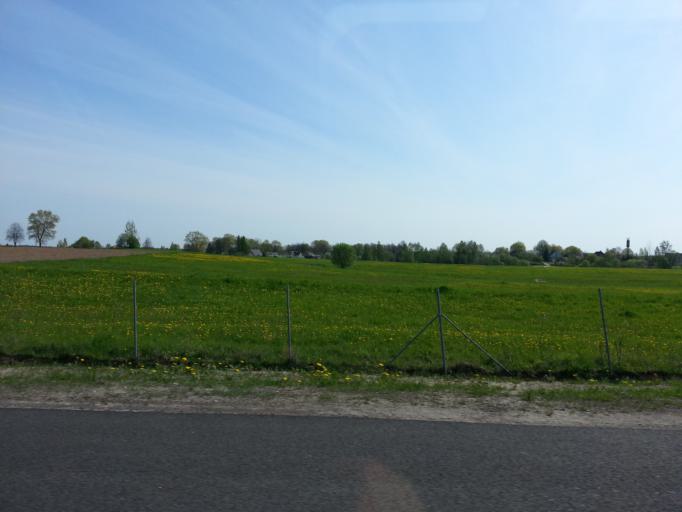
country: LT
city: Sirvintos
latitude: 55.1160
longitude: 24.8460
